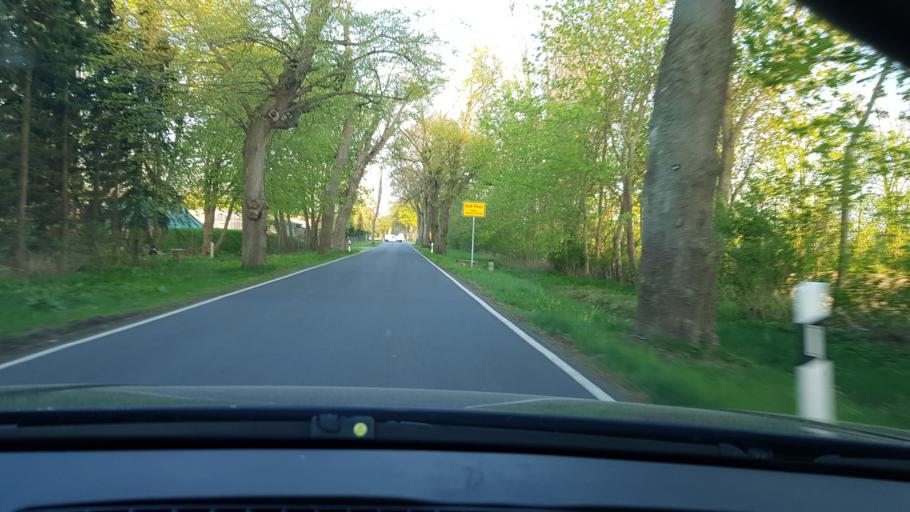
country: DE
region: Mecklenburg-Vorpommern
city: Alt-Sanitz
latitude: 53.8955
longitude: 13.5865
